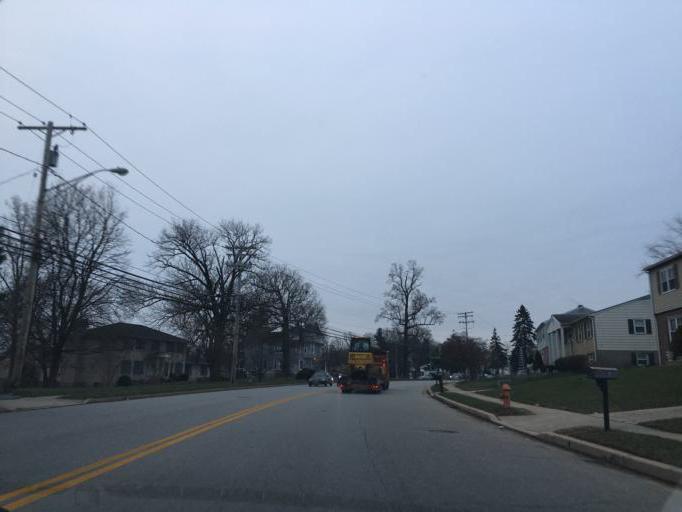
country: US
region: Maryland
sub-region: Baltimore County
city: Catonsville
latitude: 39.2920
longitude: -76.7524
